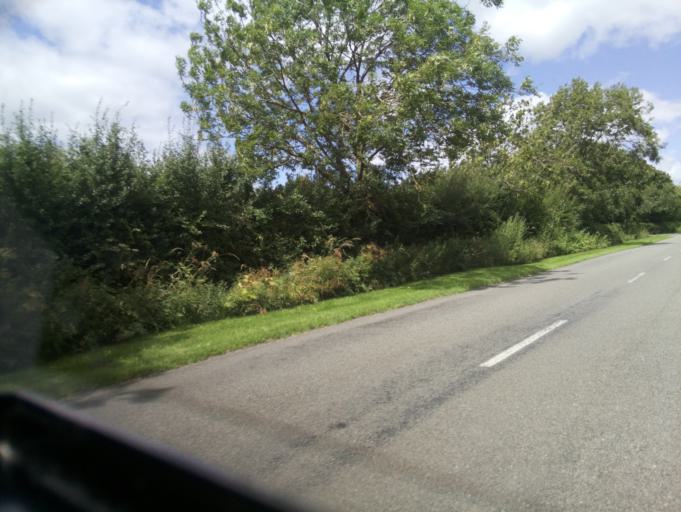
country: GB
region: England
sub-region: Nottinghamshire
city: Cotgrave
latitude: 52.8568
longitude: -1.0697
